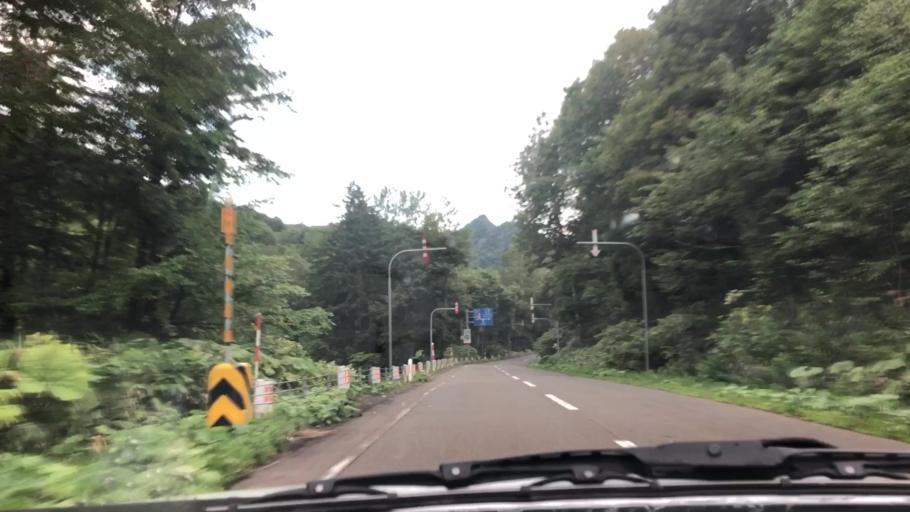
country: JP
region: Hokkaido
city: Shimo-furano
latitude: 42.9130
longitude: 142.3736
